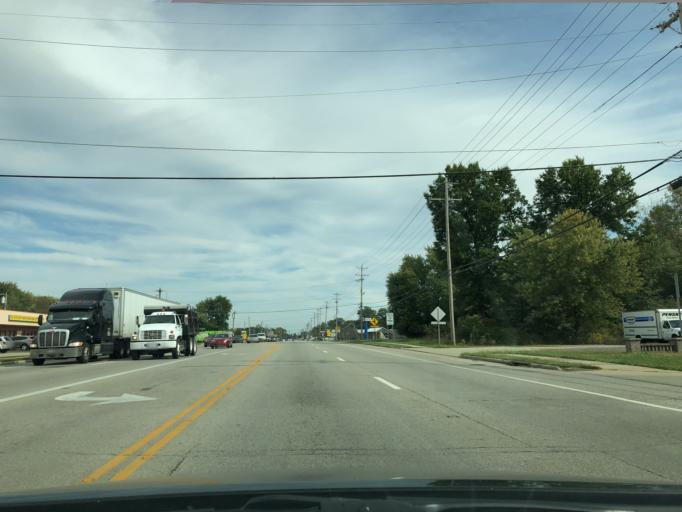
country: US
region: Ohio
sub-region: Clermont County
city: Mount Repose
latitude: 39.1998
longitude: -84.2259
